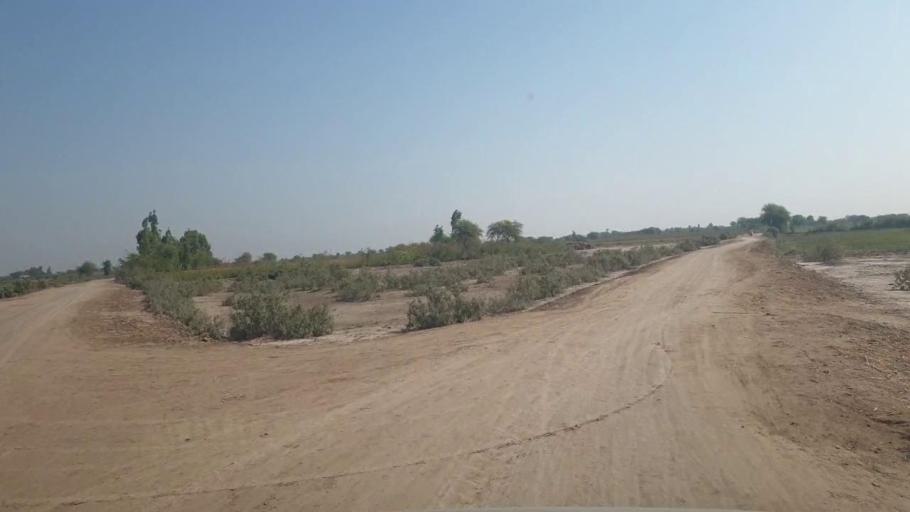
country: PK
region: Sindh
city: Badin
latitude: 24.7126
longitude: 68.8746
